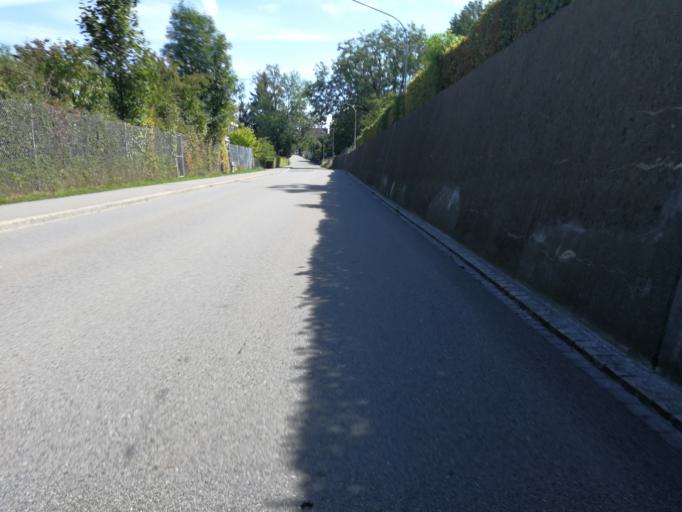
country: CH
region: Zurich
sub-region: Bezirk Horgen
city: Au / Mittel-Dorf
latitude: 47.2439
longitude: 8.6503
